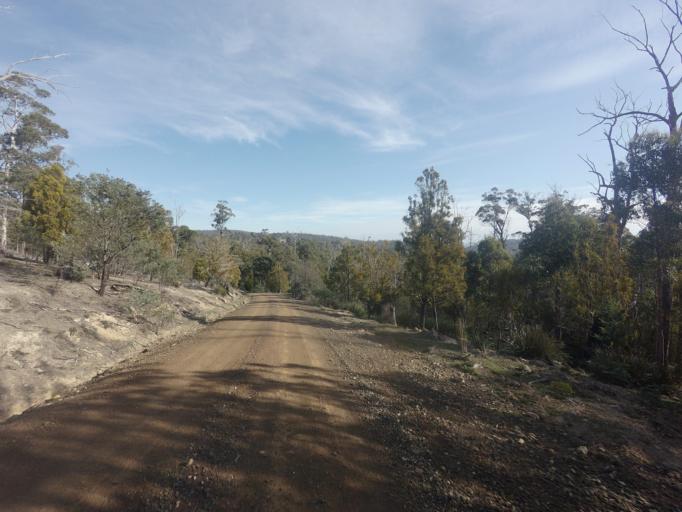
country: AU
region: Tasmania
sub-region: Sorell
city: Sorell
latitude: -42.5295
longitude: 147.4537
